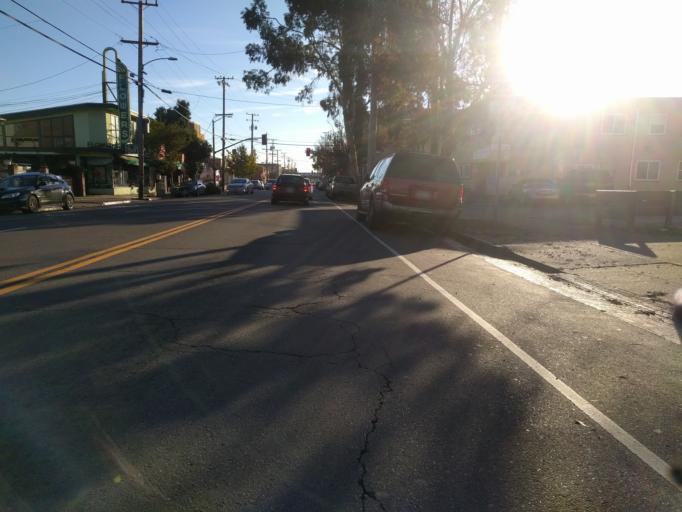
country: US
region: California
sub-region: Alameda County
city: Alameda
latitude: 37.7795
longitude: -122.2250
